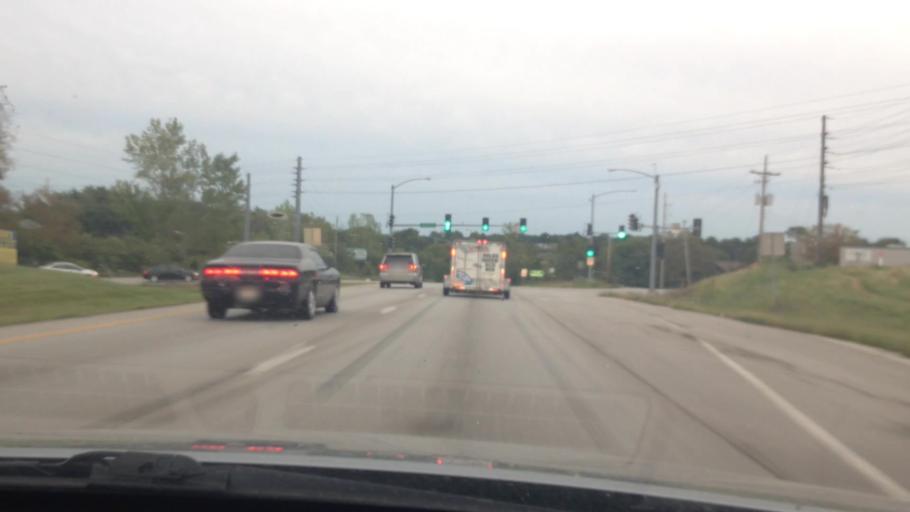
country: US
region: Missouri
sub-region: Jackson County
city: Raytown
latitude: 38.9721
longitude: -94.4427
